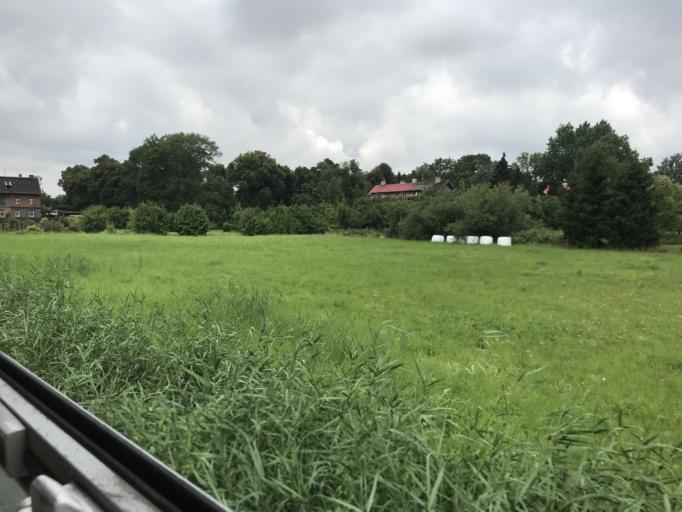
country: PL
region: Pomeranian Voivodeship
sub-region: Powiat malborski
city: Stare Pole
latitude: 54.0541
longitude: 19.2088
